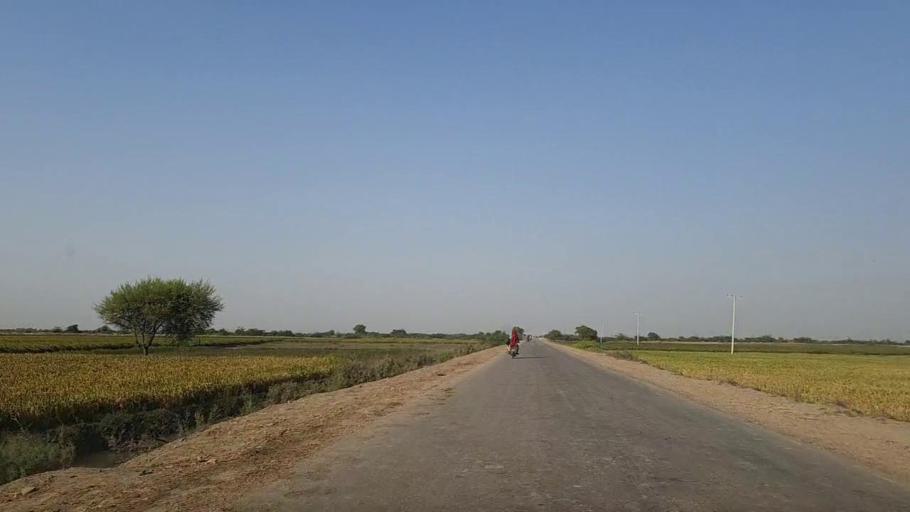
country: PK
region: Sindh
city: Mirpur Batoro
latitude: 24.5964
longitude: 68.3997
